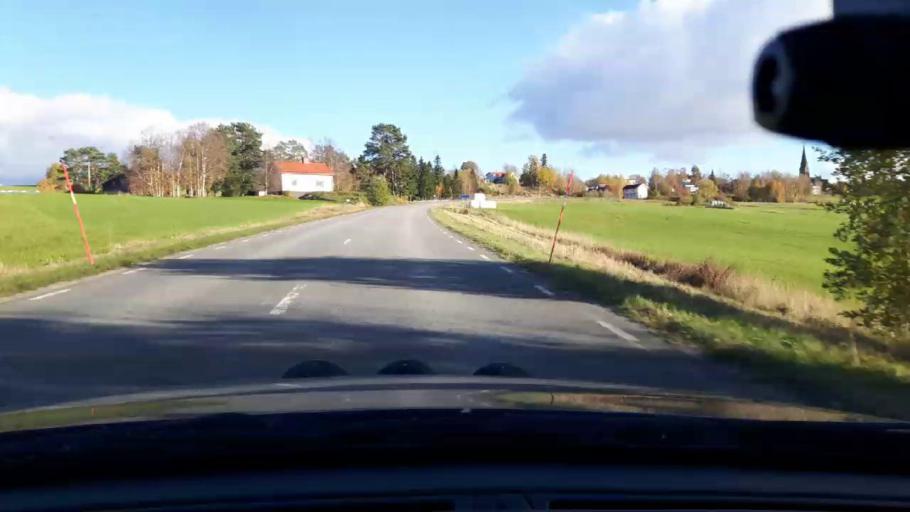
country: SE
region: Jaemtland
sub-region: Bergs Kommun
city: Hoverberg
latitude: 63.0008
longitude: 14.3836
